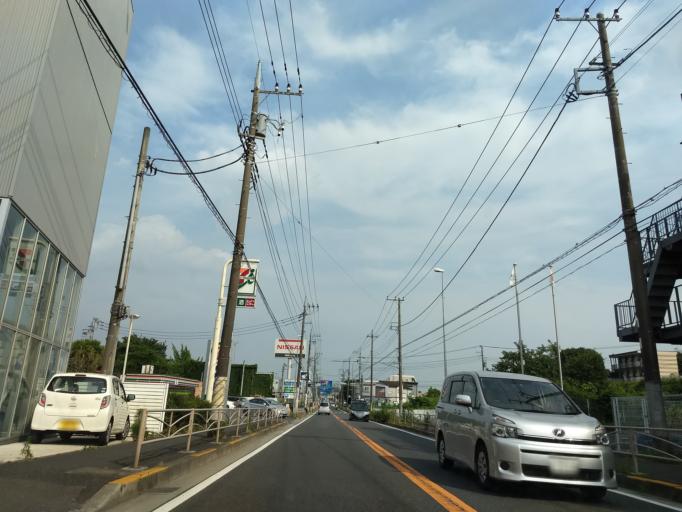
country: JP
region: Kanagawa
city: Minami-rinkan
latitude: 35.4888
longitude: 139.5175
